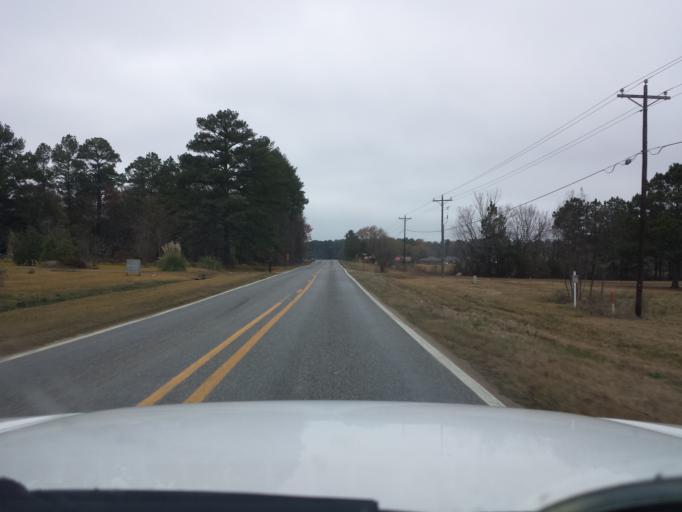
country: US
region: Mississippi
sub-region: Madison County
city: Canton
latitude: 32.4918
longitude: -89.9226
